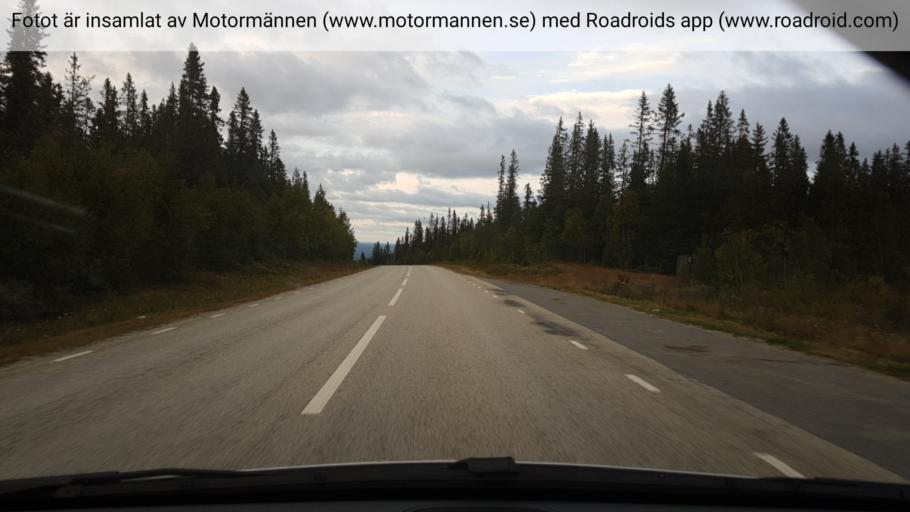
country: SE
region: Jaemtland
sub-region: Bergs Kommun
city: Hoverberg
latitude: 62.5430
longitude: 14.2594
